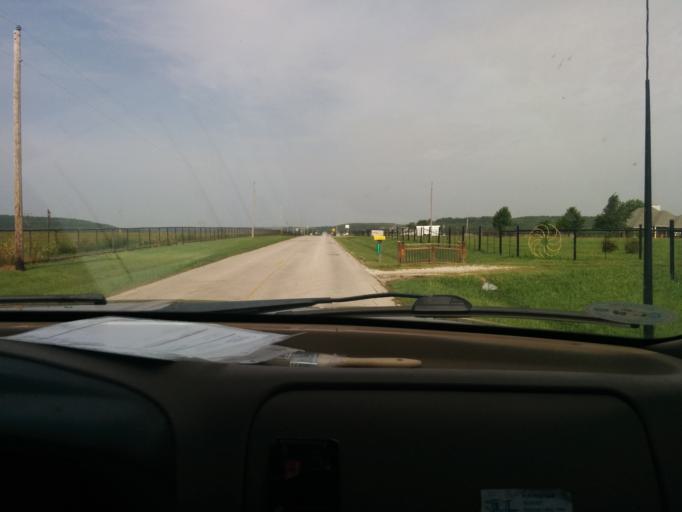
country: US
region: Oklahoma
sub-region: Tulsa County
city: Sperry
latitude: 36.3035
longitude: -96.0632
